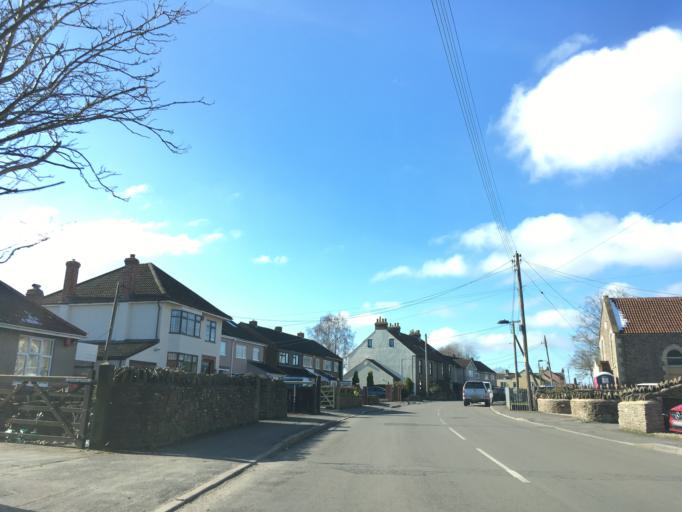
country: GB
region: England
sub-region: South Gloucestershire
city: Winterbourne
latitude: 51.5312
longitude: -2.4918
